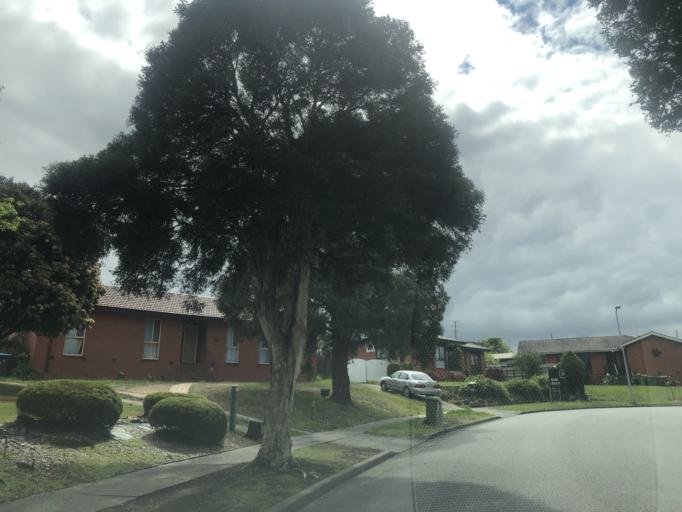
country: AU
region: Victoria
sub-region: Casey
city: Endeavour Hills
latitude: -37.9752
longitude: 145.2430
